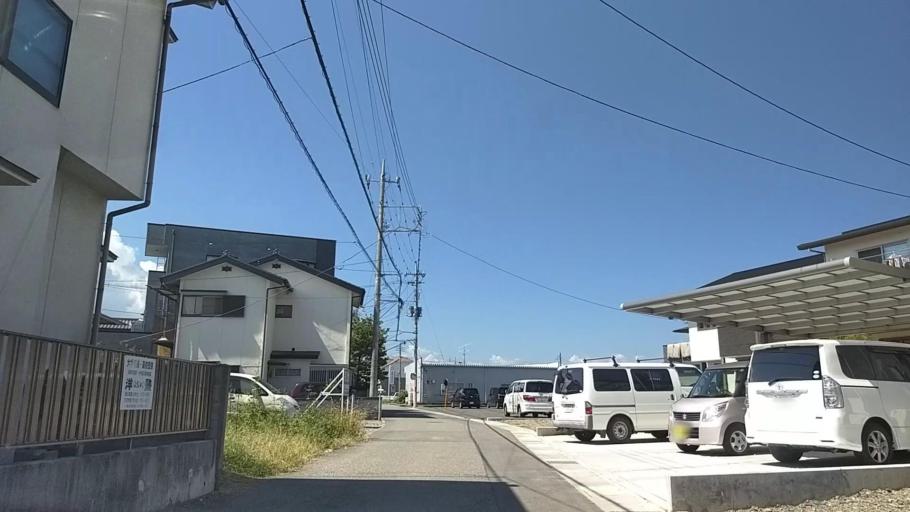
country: JP
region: Yamanashi
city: Ryuo
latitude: 35.6619
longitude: 138.5228
